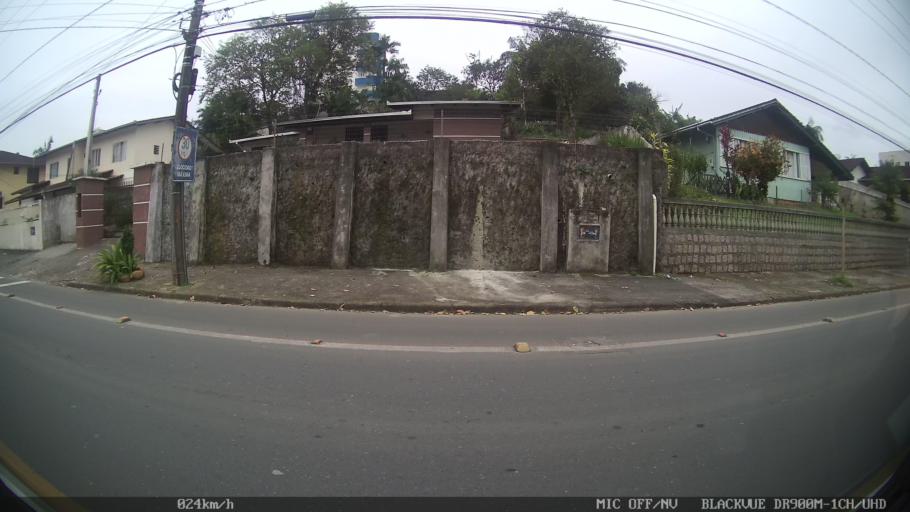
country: BR
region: Santa Catarina
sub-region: Joinville
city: Joinville
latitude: -26.2713
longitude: -48.8388
